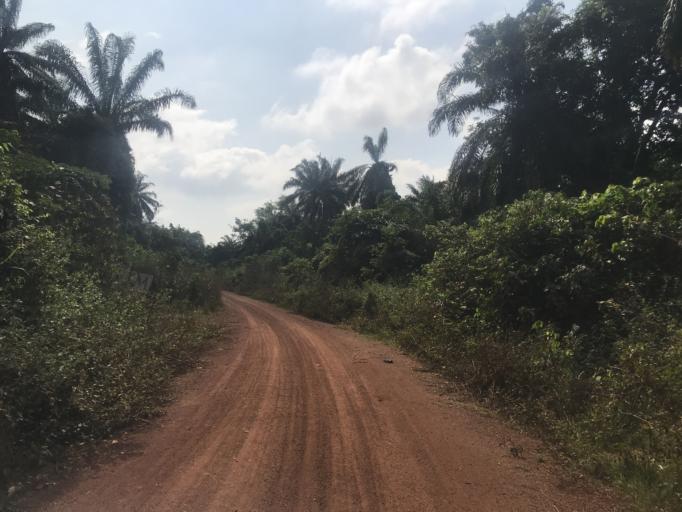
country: NG
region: Osun
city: Ibokun
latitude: 7.8143
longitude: 4.6464
